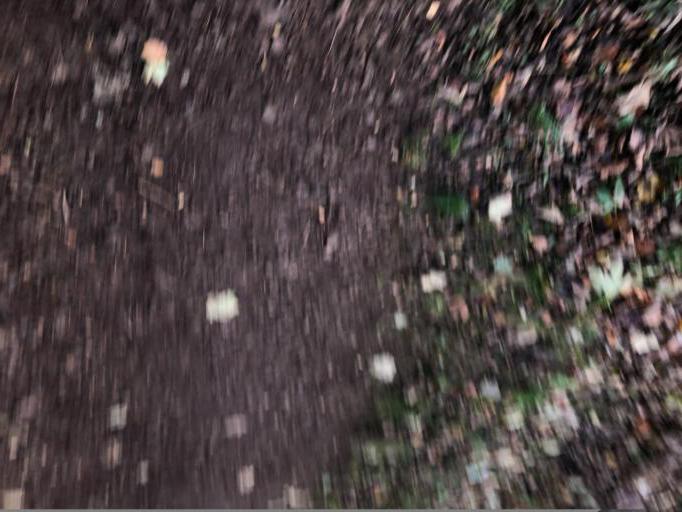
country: GB
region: Scotland
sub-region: Edinburgh
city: Colinton
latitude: 55.8931
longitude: -3.2609
